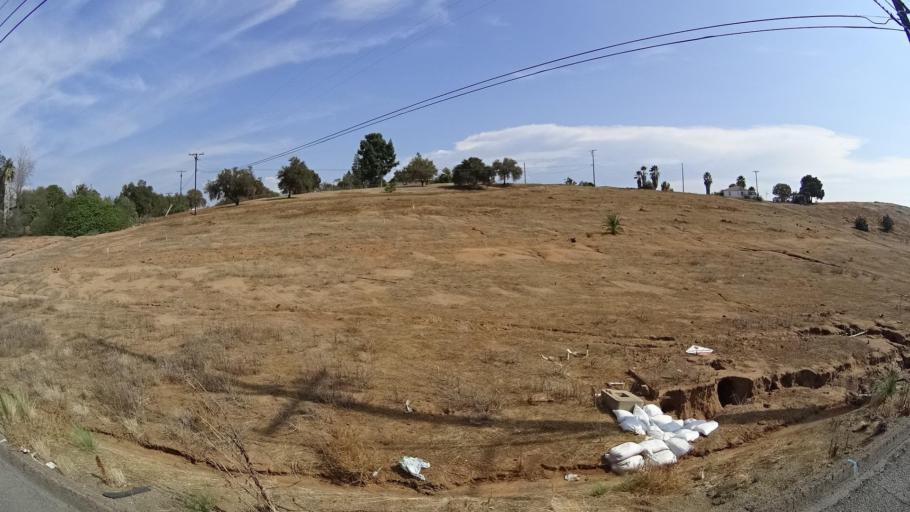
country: US
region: California
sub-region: San Diego County
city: Escondido
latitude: 33.1013
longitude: -117.0563
